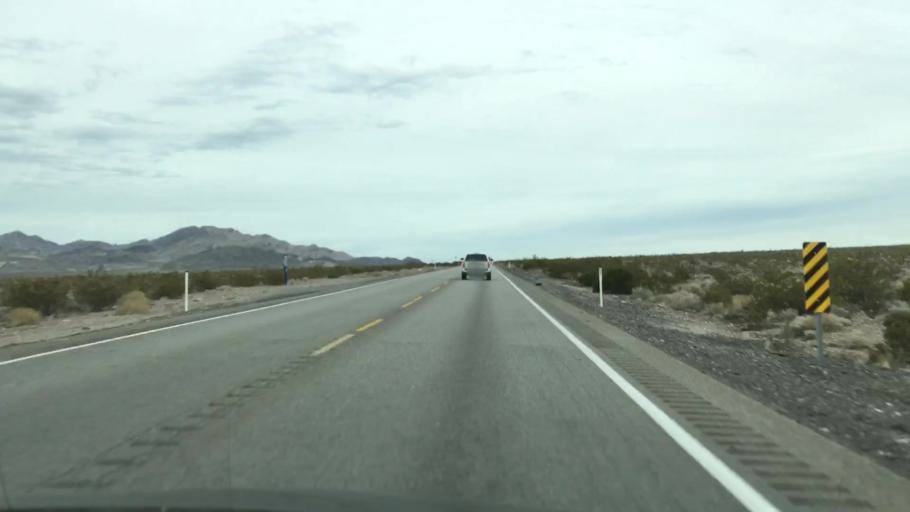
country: US
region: Nevada
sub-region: Nye County
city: Pahrump
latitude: 36.5924
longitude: -116.0291
